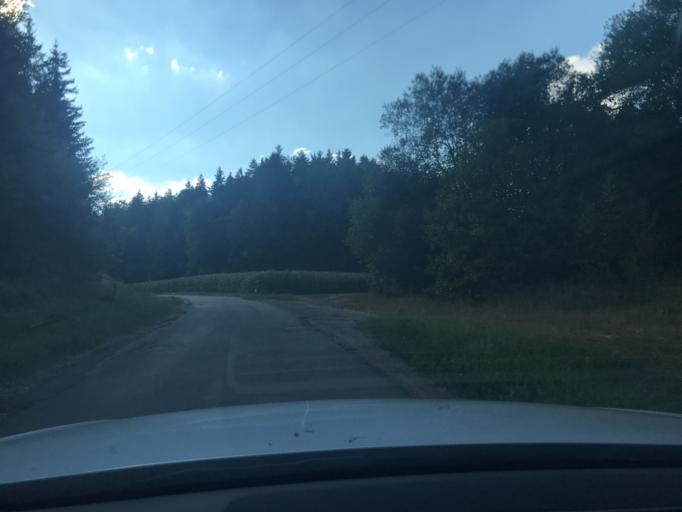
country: DE
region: Bavaria
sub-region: Upper Palatinate
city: Auerbach
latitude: 49.7373
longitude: 11.5980
